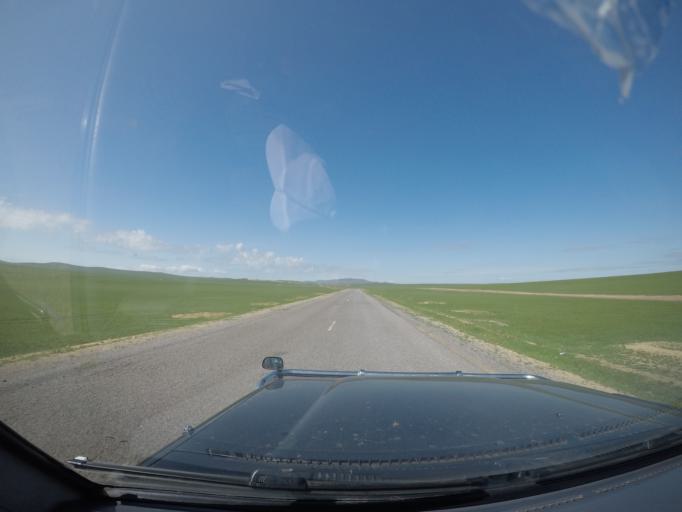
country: MN
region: Suhbaatar
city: Bayasgalant
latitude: 47.3428
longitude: 111.5858
